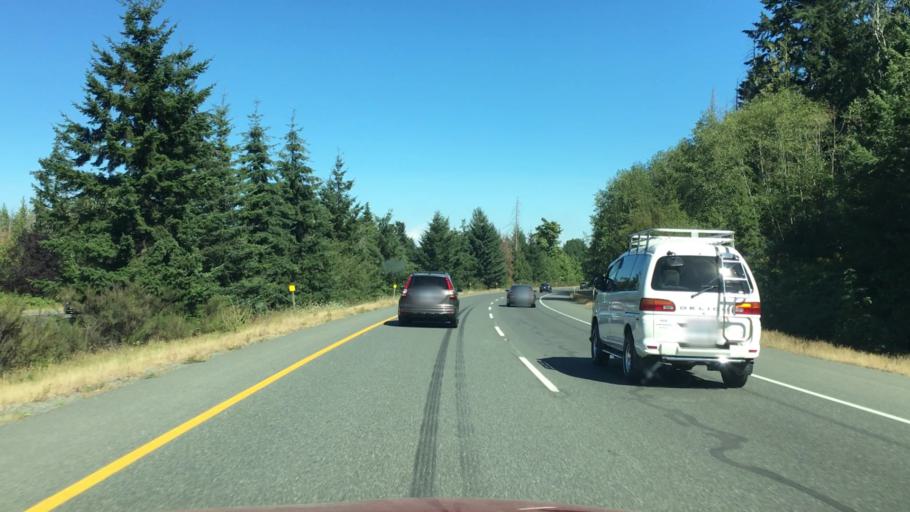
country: CA
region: British Columbia
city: Nanaimo
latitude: 49.1353
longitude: -123.9395
